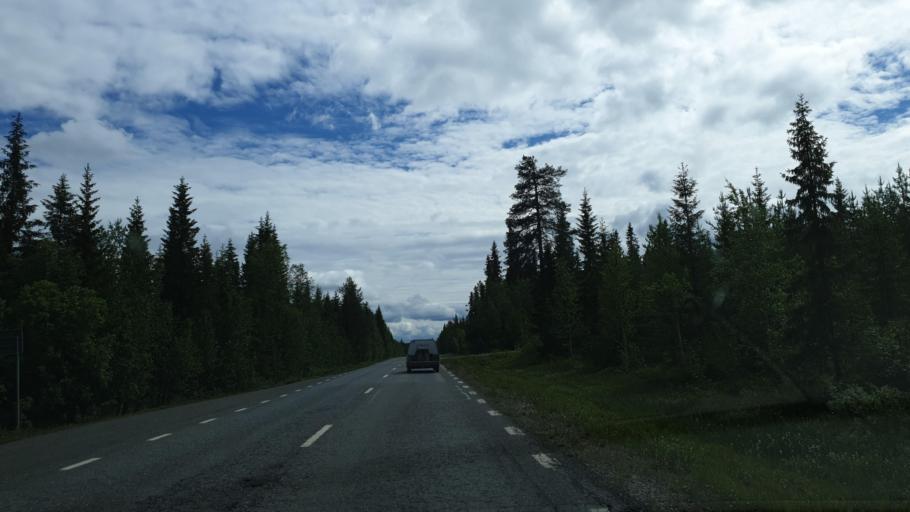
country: SE
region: Vaesterbotten
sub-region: Vilhelmina Kommun
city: Sjoberg
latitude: 64.8754
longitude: 15.8793
